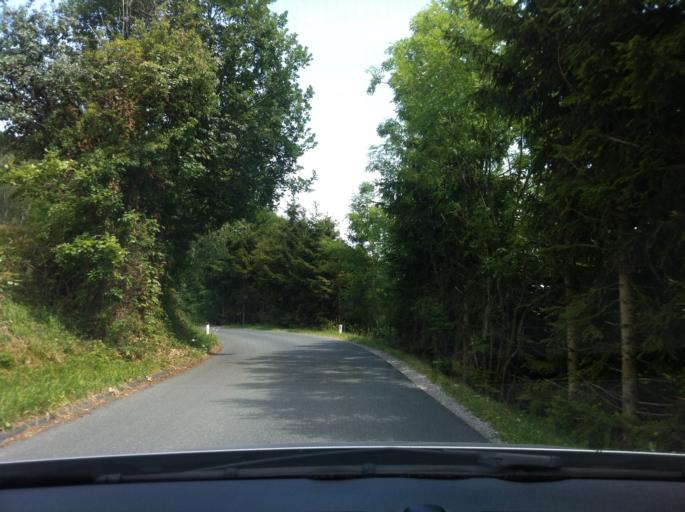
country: AT
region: Styria
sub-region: Politischer Bezirk Hartberg-Fuerstenfeld
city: Siegersdorf bei Herberstein
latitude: 47.2179
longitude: 15.7568
